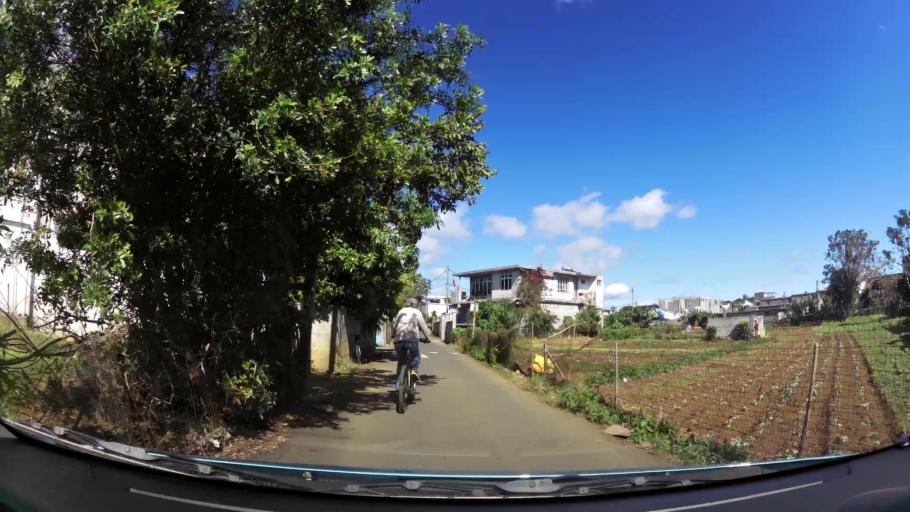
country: MU
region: Plaines Wilhems
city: Vacoas
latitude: -20.3175
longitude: 57.4871
